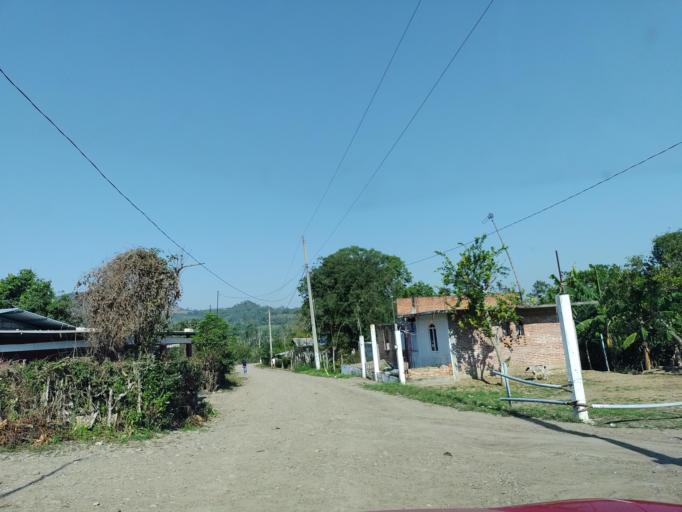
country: MX
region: Veracruz
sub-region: Papantla
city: Polutla
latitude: 20.5159
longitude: -97.2434
